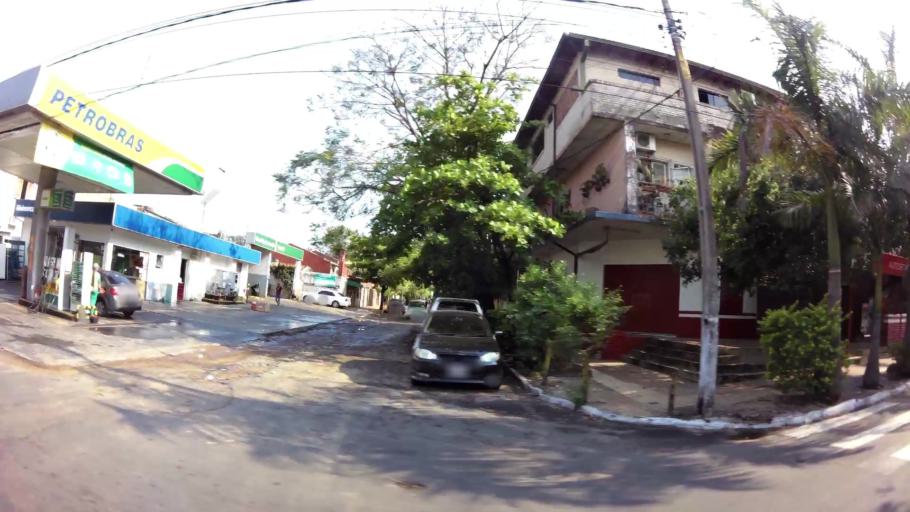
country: PY
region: Presidente Hayes
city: Nanawa
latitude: -25.2905
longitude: -57.6650
